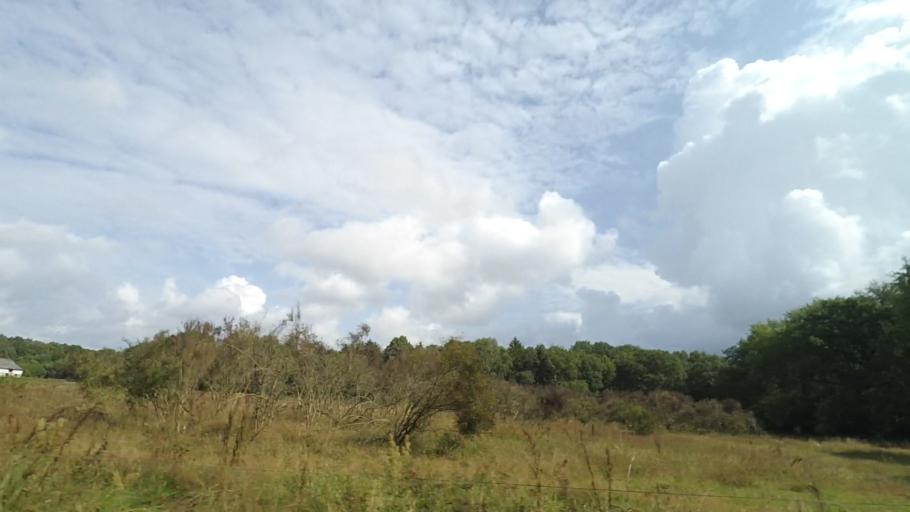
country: DK
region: Central Jutland
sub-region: Syddjurs Kommune
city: Ryomgard
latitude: 56.4613
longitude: 10.5320
